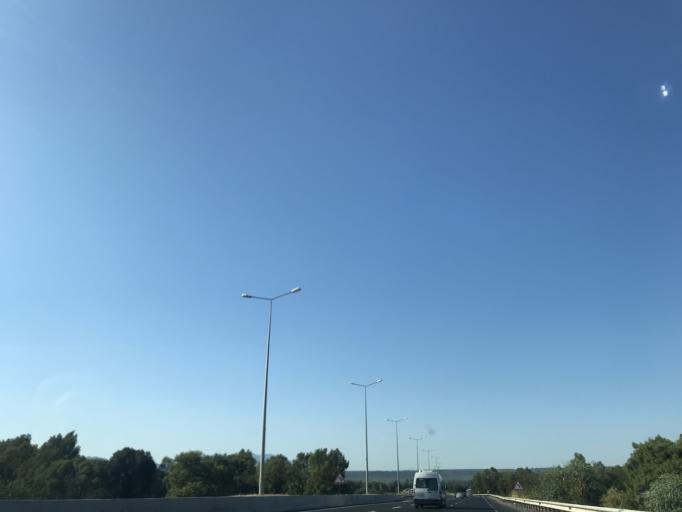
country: TR
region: Antalya
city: Cakirlar
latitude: 36.8721
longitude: 30.6105
